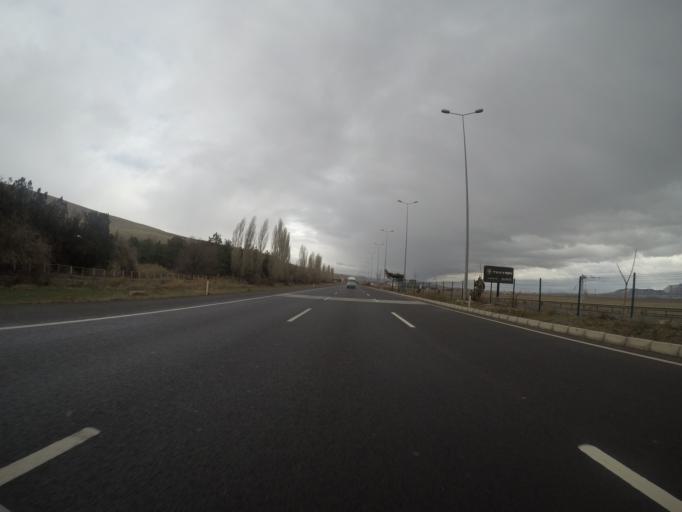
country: TR
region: Kayseri
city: Incesu
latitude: 38.7263
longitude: 35.2786
